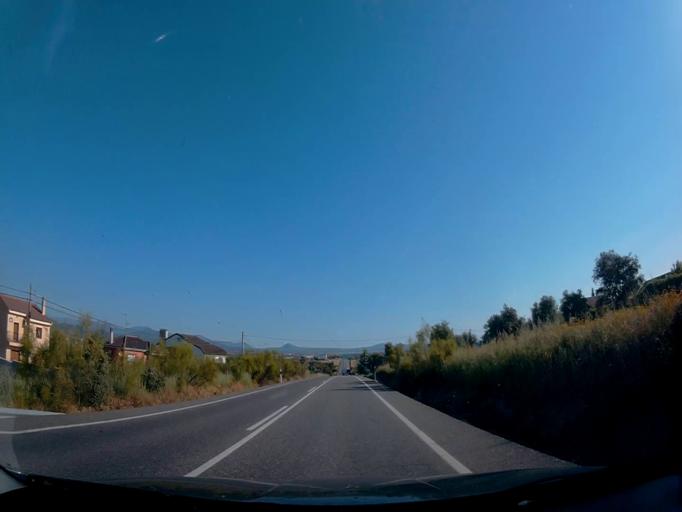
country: ES
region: Castille-La Mancha
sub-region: Province of Toledo
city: Escalona
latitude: 40.1397
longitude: -4.4038
